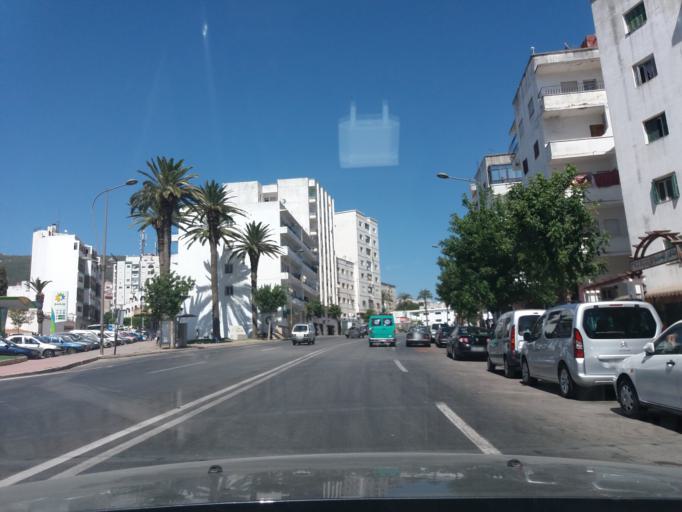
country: MA
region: Tanger-Tetouan
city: Tetouan
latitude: 35.5696
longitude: -5.3877
